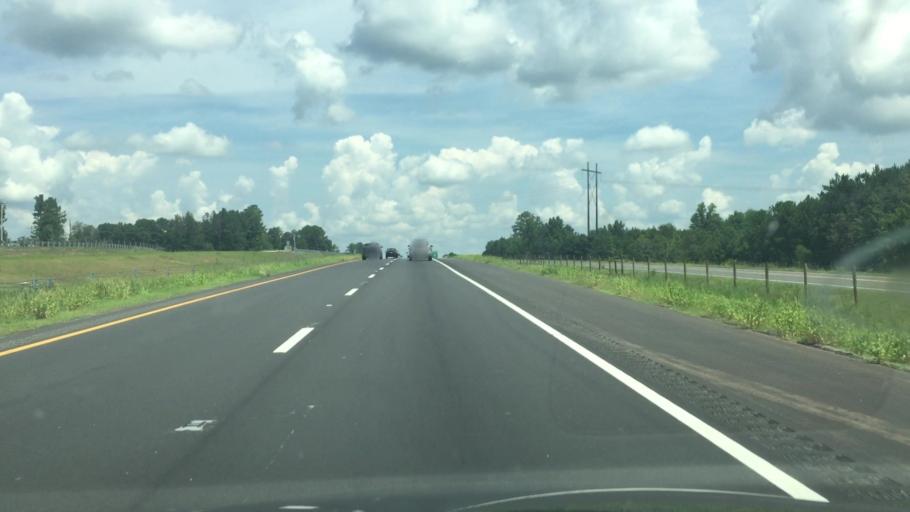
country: US
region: North Carolina
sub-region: Richmond County
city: Ellerbe
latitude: 35.0338
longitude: -79.7690
